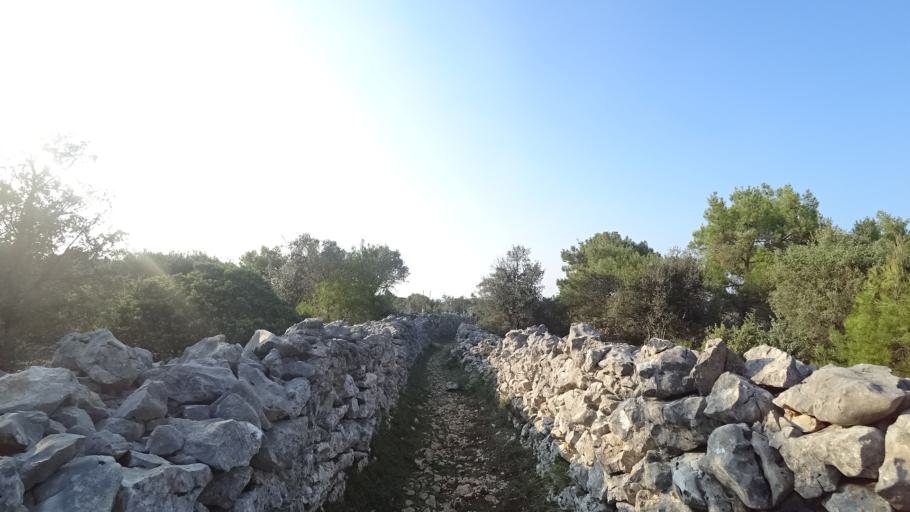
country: HR
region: Primorsko-Goranska
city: Mali Losinj
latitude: 44.5225
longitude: 14.4770
